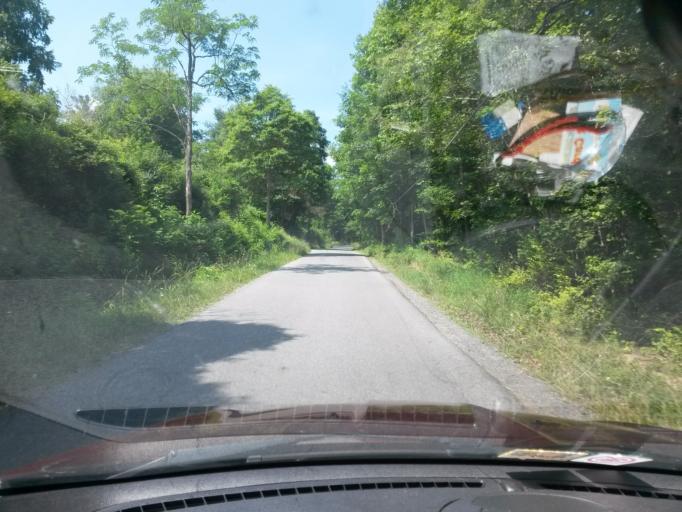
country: US
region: West Virginia
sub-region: Mercer County
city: Princeton
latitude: 37.3979
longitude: -81.1102
